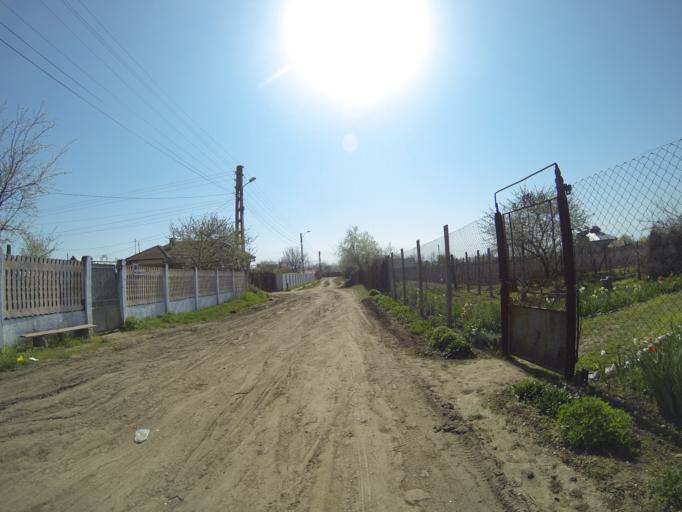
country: RO
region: Dolj
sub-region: Comuna Segarcea
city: Segarcea
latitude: 44.0929
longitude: 23.7321
